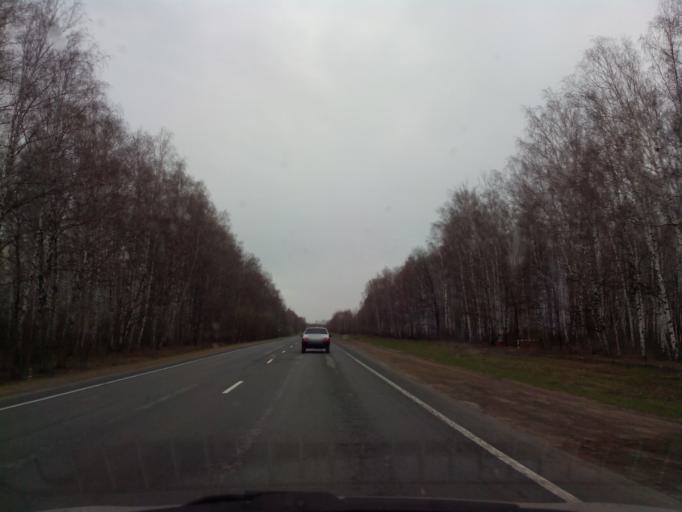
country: RU
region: Tambov
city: Michurinsk
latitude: 53.0737
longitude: 40.4254
